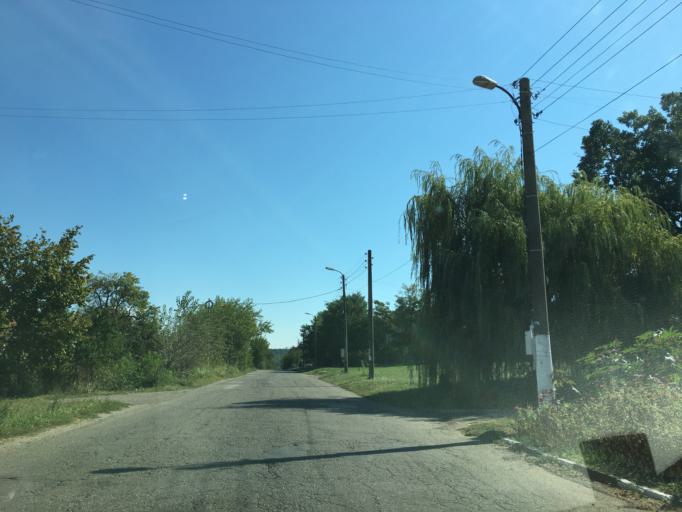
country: RO
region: Dolj
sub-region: Comuna Desa
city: Desa
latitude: 43.7679
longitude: 23.0067
